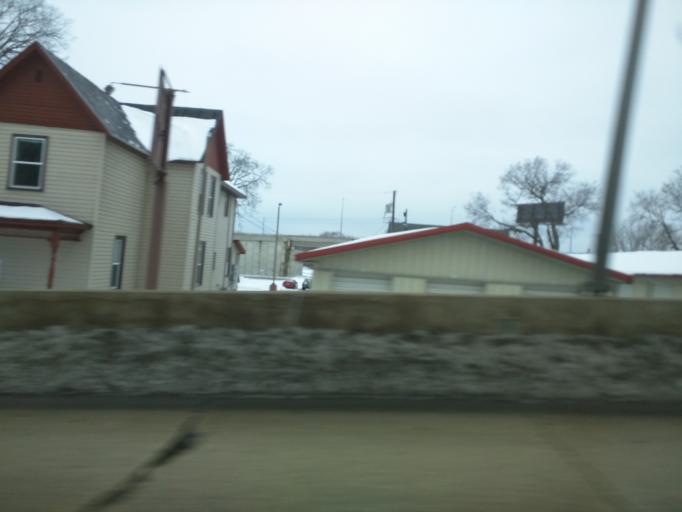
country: US
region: Wisconsin
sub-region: La Crosse County
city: North La Crosse
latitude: 43.8319
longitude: -91.2481
